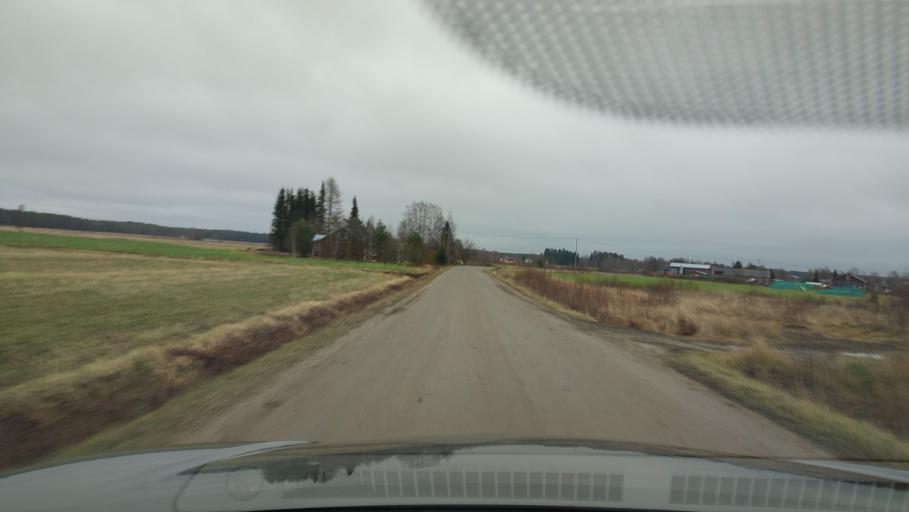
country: FI
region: Southern Ostrobothnia
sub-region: Suupohja
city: Isojoki
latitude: 62.1926
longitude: 21.9524
